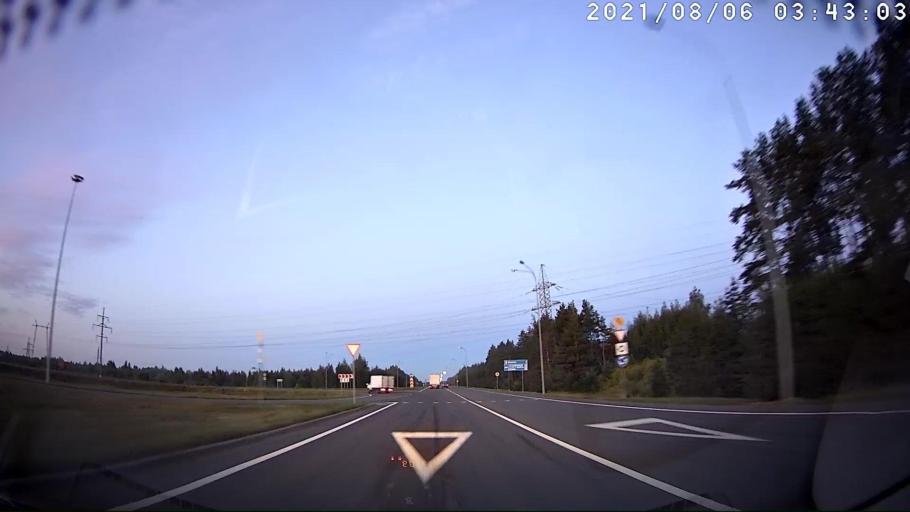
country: RU
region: Mariy-El
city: Volzhsk
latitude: 55.9133
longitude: 48.3659
